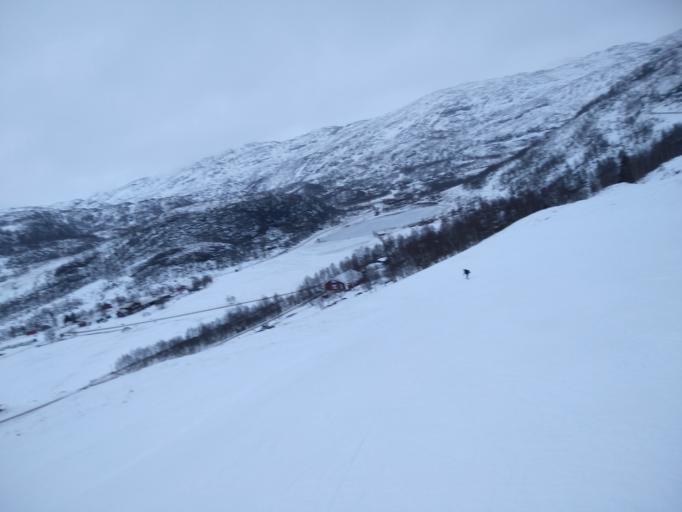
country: NO
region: Vest-Agder
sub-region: Sirdal
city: Tonstad
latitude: 59.0220
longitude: 6.9185
